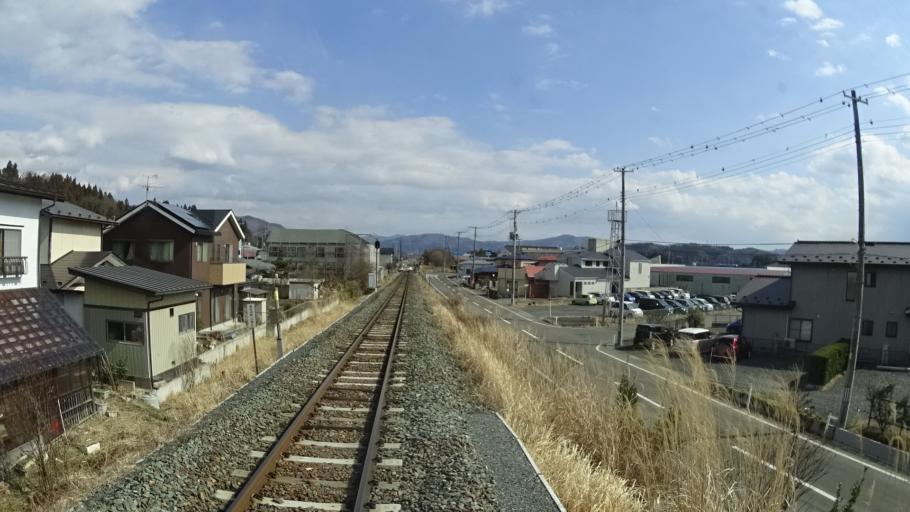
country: JP
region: Iwate
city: Hanamaki
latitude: 39.3852
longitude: 141.2296
